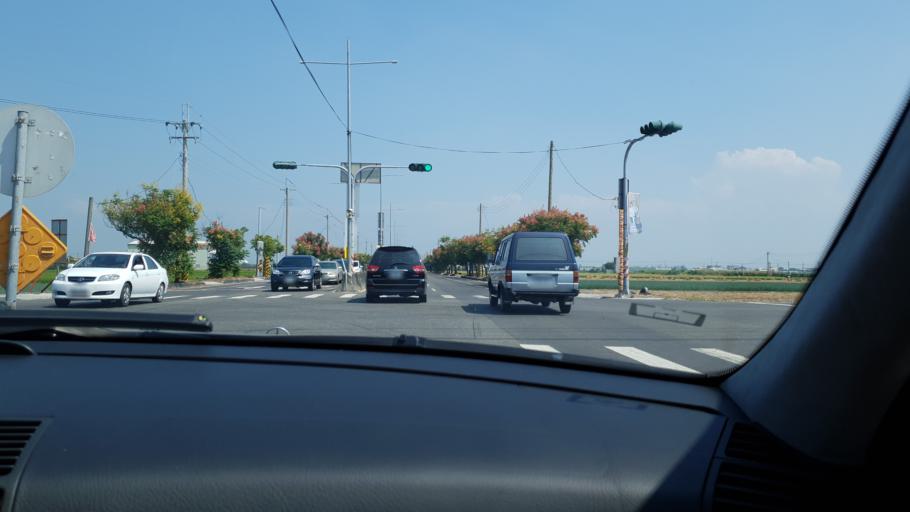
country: TW
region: Taiwan
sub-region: Yunlin
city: Douliu
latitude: 23.7357
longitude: 120.4576
